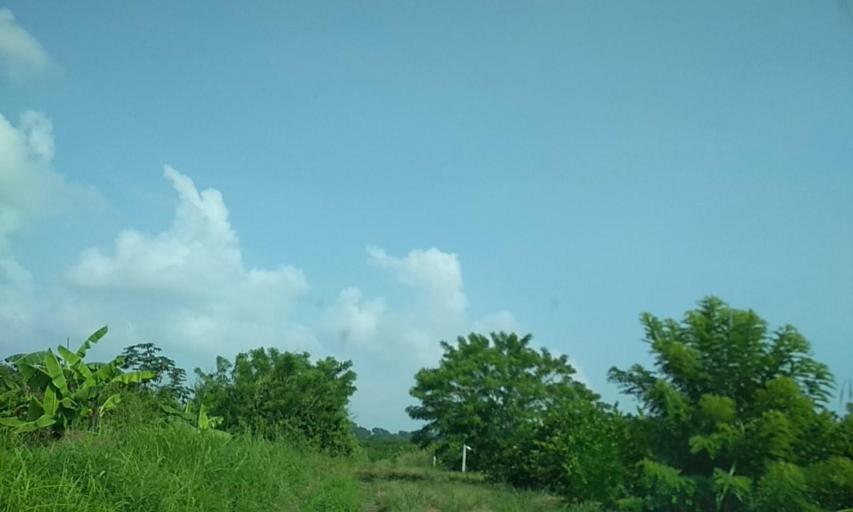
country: MX
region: Veracruz
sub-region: Martinez de la Torre
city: El Progreso
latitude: 20.1475
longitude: -97.0594
